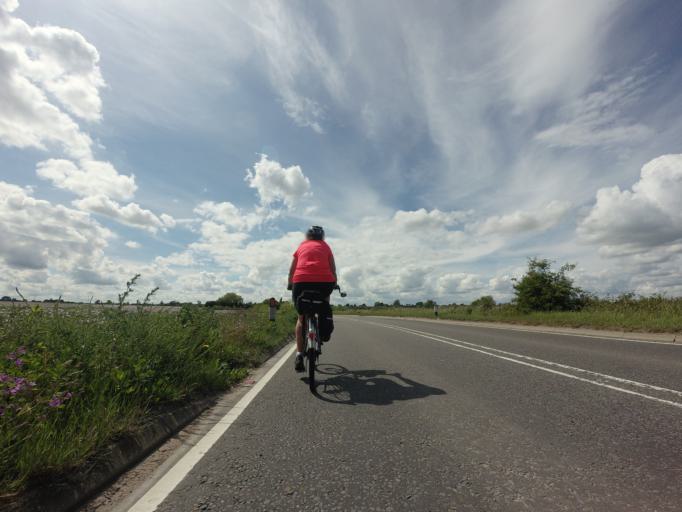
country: GB
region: England
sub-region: Medway
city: Allhallows
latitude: 51.4510
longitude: 0.6441
